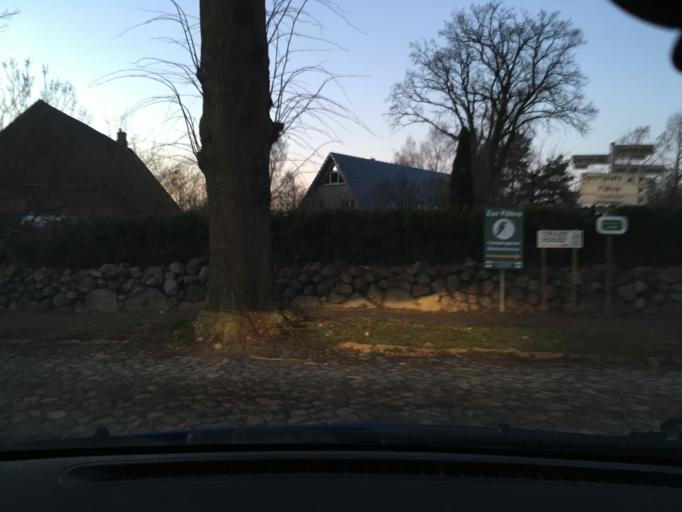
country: DE
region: Schleswig-Holstein
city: Fitzen
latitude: 53.4945
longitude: 10.6465
